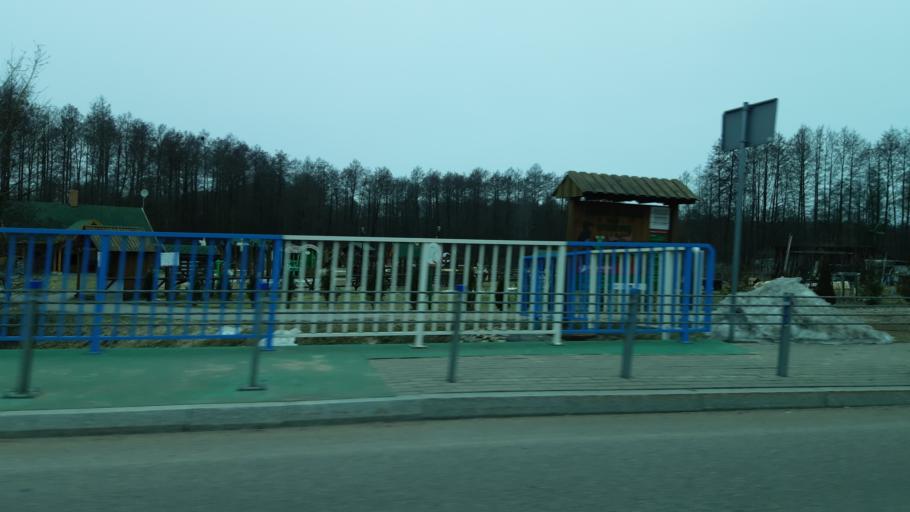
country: PL
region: Podlasie
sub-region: Suwalki
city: Suwalki
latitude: 54.3237
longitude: 22.9692
